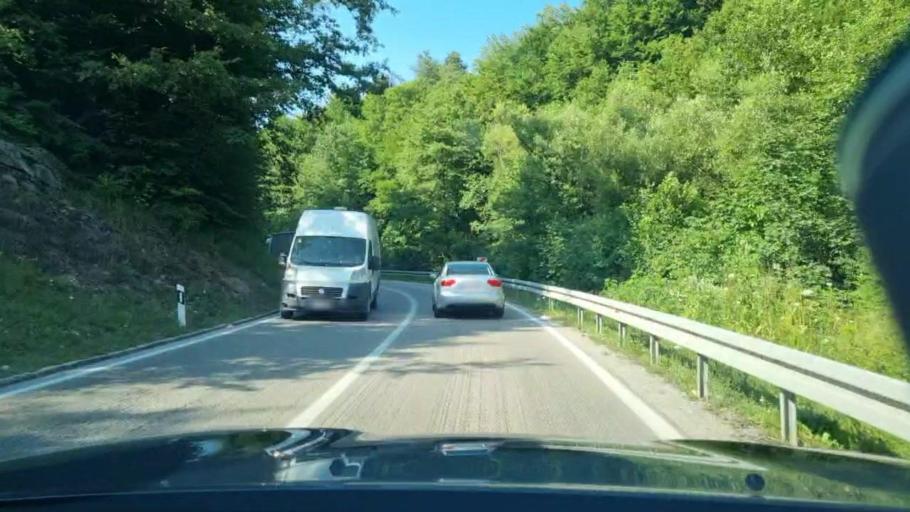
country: BA
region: Federation of Bosnia and Herzegovina
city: Skokovi
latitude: 45.0066
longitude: 15.9056
